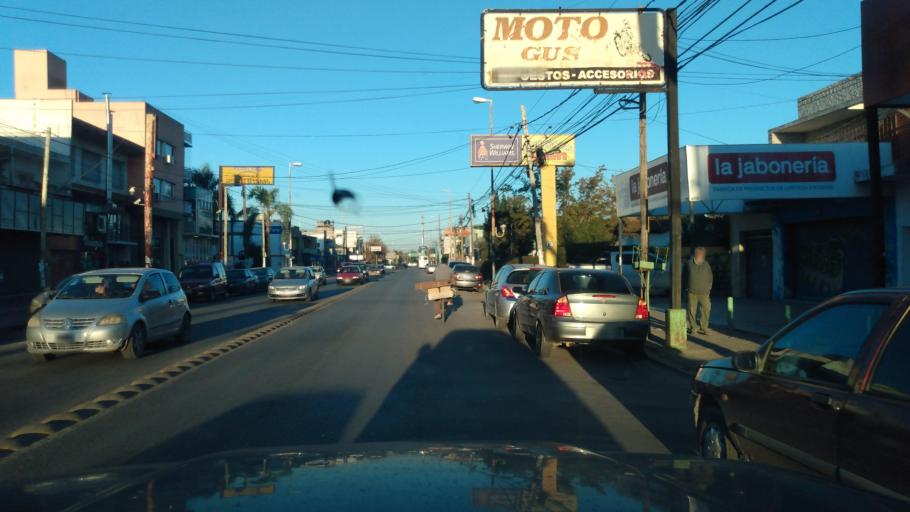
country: AR
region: Buenos Aires
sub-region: Partido de Merlo
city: Merlo
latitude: -34.6568
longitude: -58.7625
